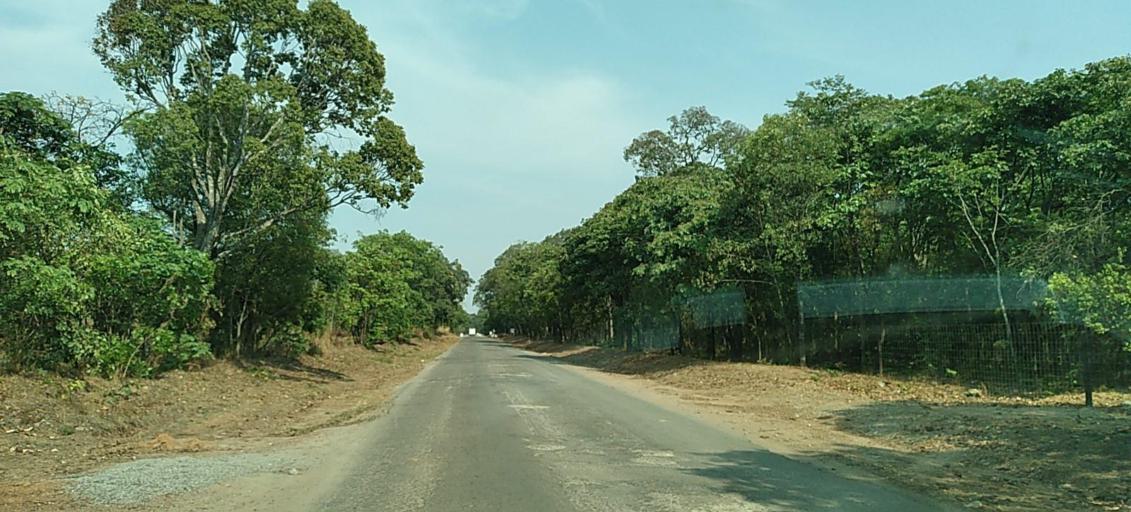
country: ZM
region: Copperbelt
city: Chililabombwe
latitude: -12.3048
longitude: 27.7841
